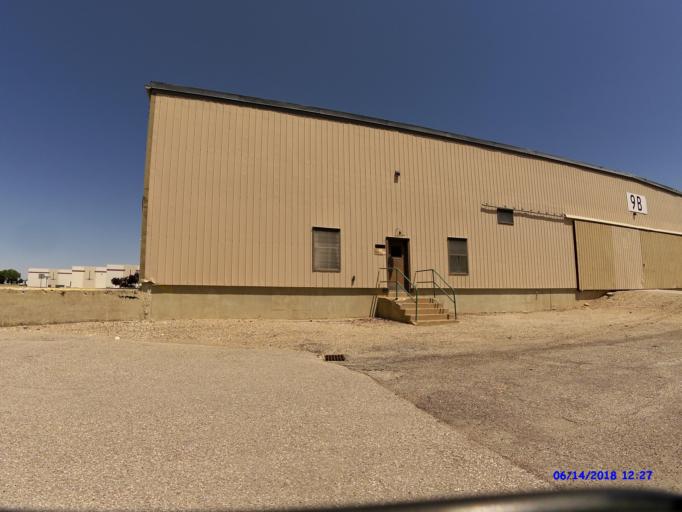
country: US
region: Utah
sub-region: Weber County
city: Harrisville
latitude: 41.2625
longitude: -111.9996
